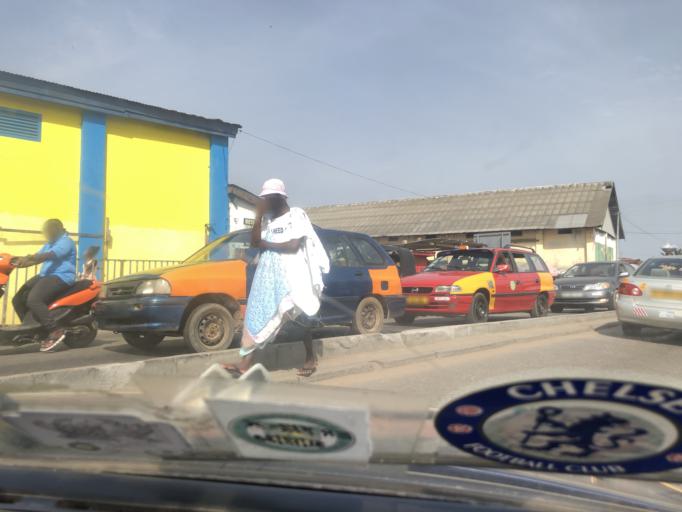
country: GH
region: Eastern
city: Koforidua
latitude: 6.0947
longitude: -0.2604
